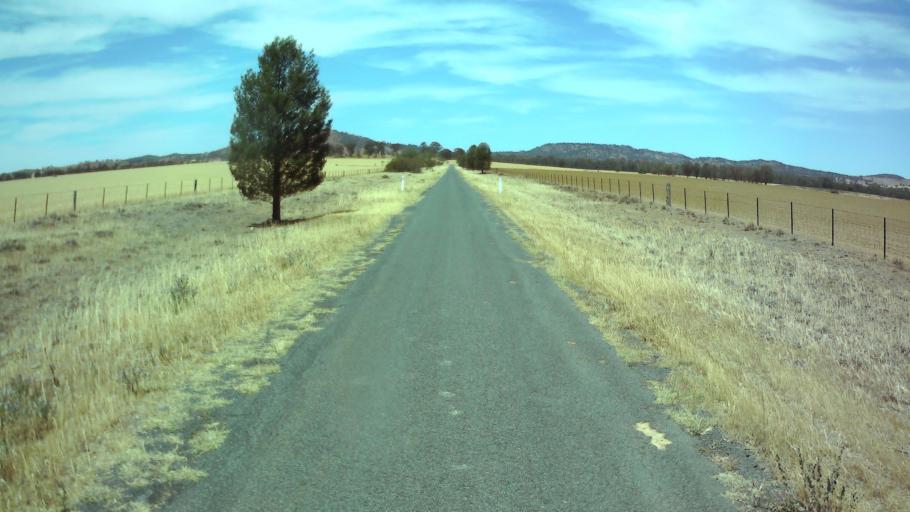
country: AU
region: New South Wales
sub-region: Weddin
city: Grenfell
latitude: -33.7597
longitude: 148.1075
